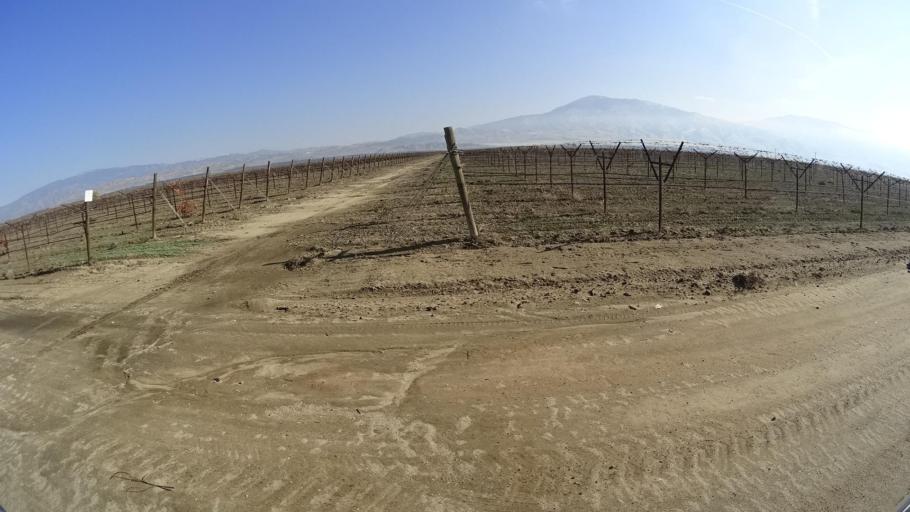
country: US
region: California
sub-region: Kern County
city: Arvin
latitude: 35.2549
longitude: -118.8069
